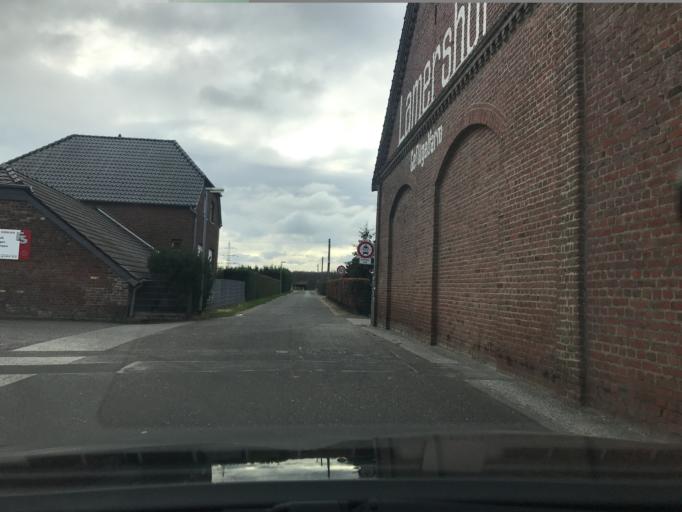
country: DE
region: North Rhine-Westphalia
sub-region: Regierungsbezirk Dusseldorf
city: Krefeld
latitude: 51.4025
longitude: 6.5262
